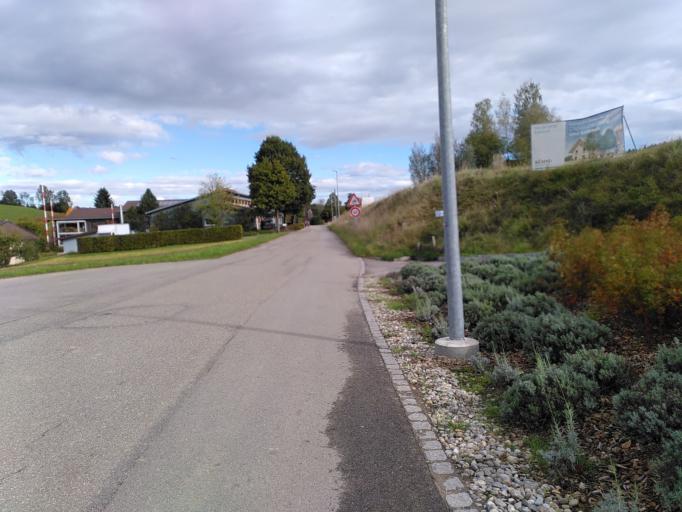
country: CH
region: Bern
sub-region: Emmental District
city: Wynigen
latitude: 47.1015
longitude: 7.6424
